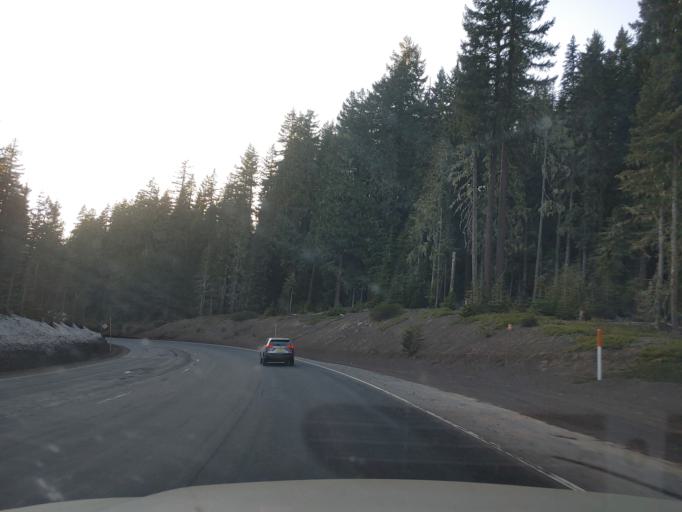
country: US
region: Oregon
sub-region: Lane County
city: Oakridge
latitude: 43.6207
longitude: -122.0688
